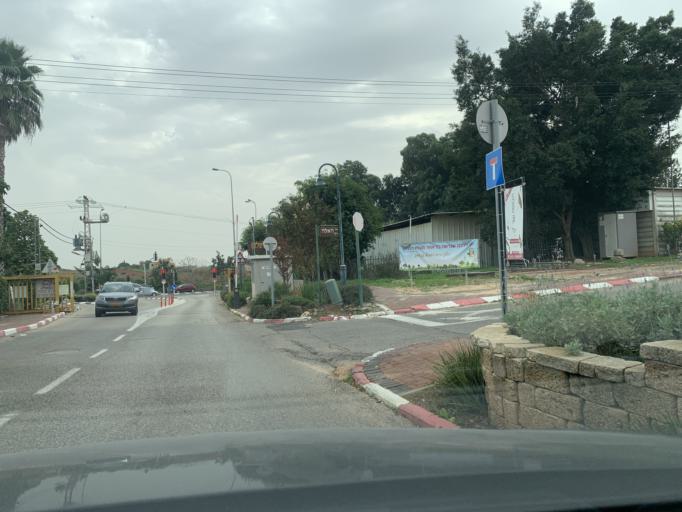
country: IL
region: Central District
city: Kfar Saba
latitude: 32.1933
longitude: 34.9086
